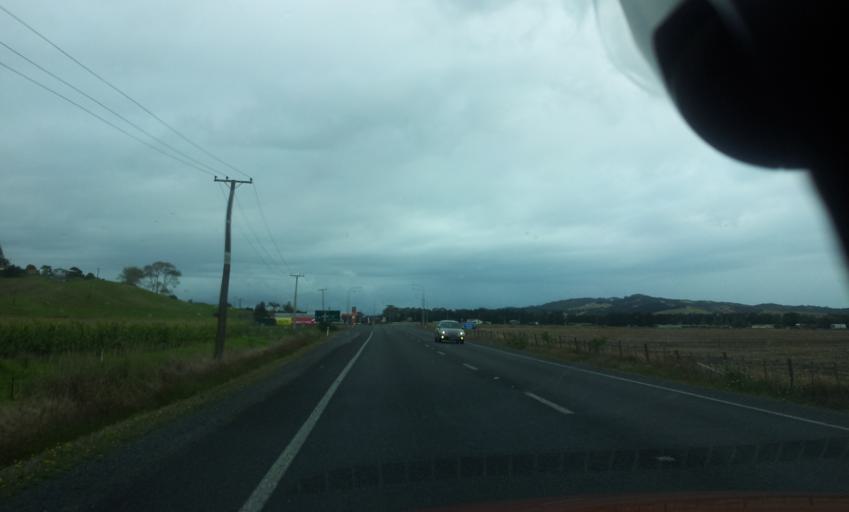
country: NZ
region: Northland
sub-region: Whangarei
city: Ruakaka
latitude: -35.8950
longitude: 174.4370
